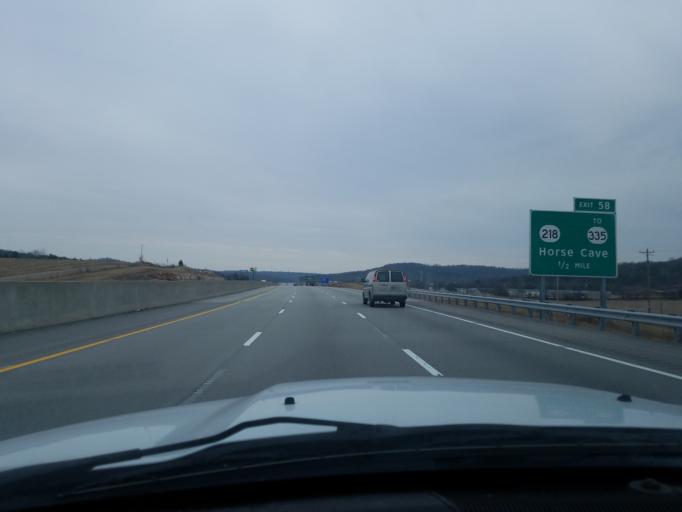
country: US
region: Kentucky
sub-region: Hart County
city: Horse Cave
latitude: 37.2136
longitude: -85.9360
